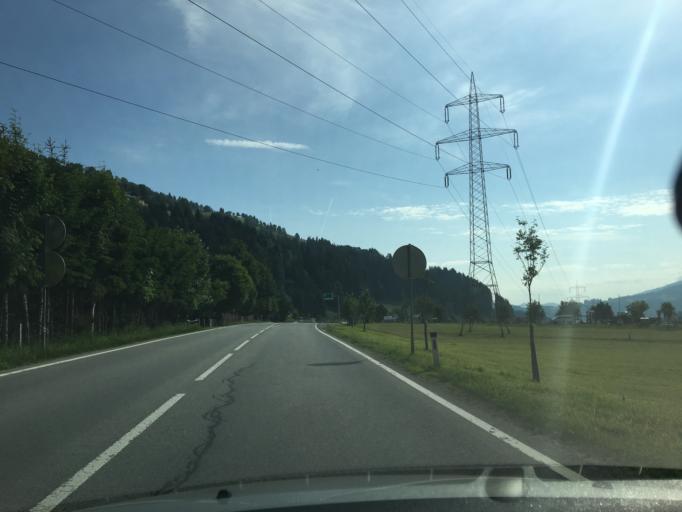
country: AT
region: Salzburg
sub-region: Politischer Bezirk Sankt Johann im Pongau
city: Wagrain
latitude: 47.3577
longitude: 13.3402
